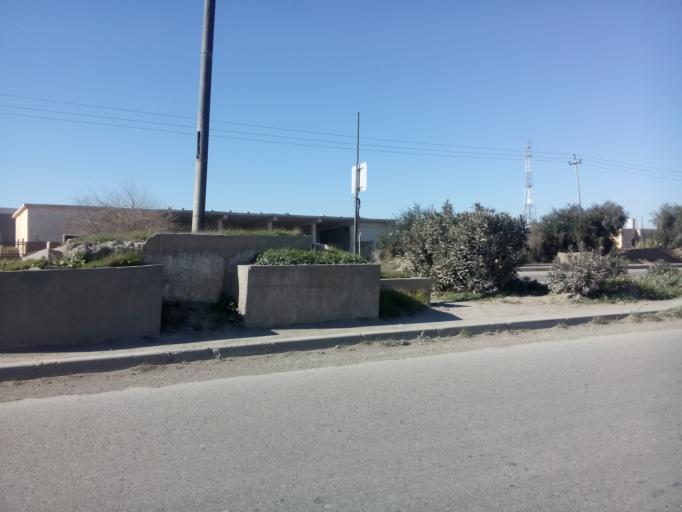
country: IQ
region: Muhafazat Kirkuk
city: Daquq
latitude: 35.1382
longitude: 44.4427
